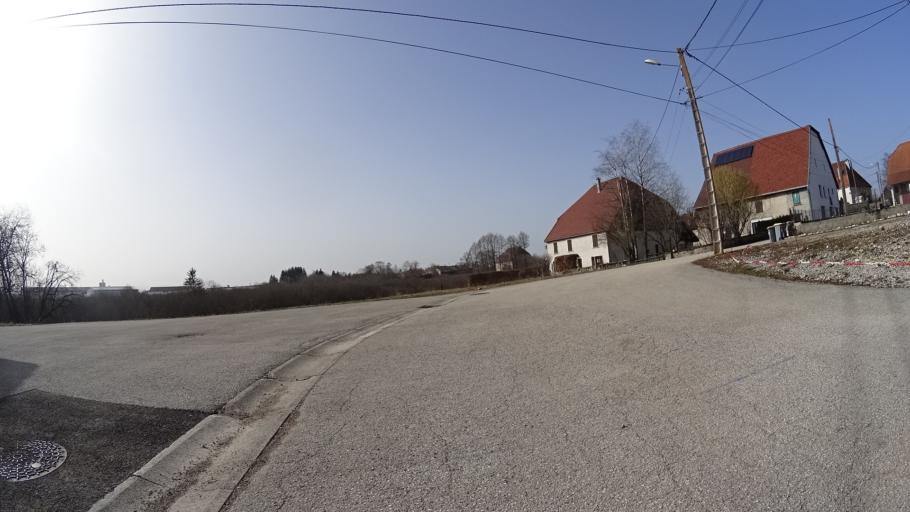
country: FR
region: Franche-Comte
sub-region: Departement du Doubs
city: Frasne
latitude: 46.8578
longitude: 6.1673
